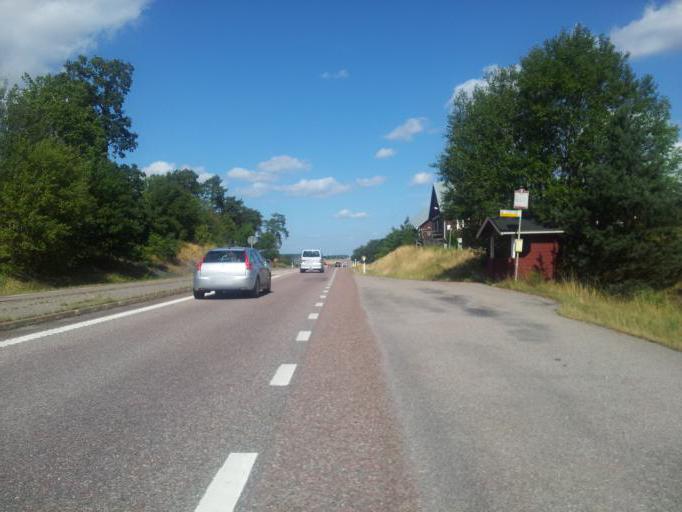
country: SE
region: Uppsala
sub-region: Uppsala Kommun
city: Gamla Uppsala
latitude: 59.9055
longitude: 17.6100
